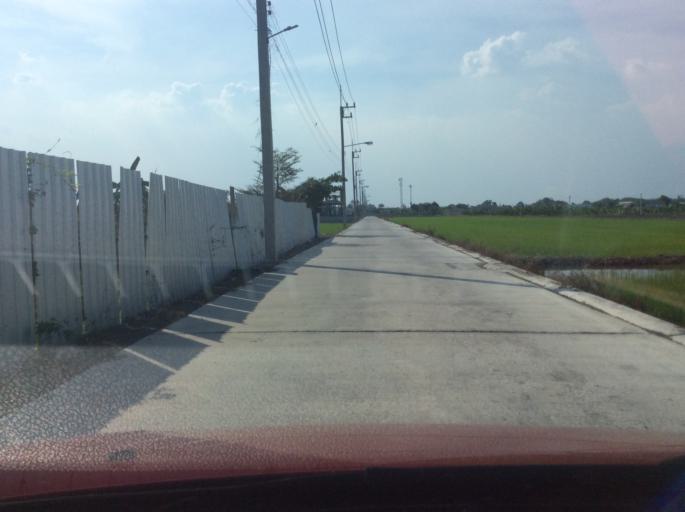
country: TH
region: Pathum Thani
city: Lam Luk Ka
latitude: 13.9677
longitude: 100.7357
